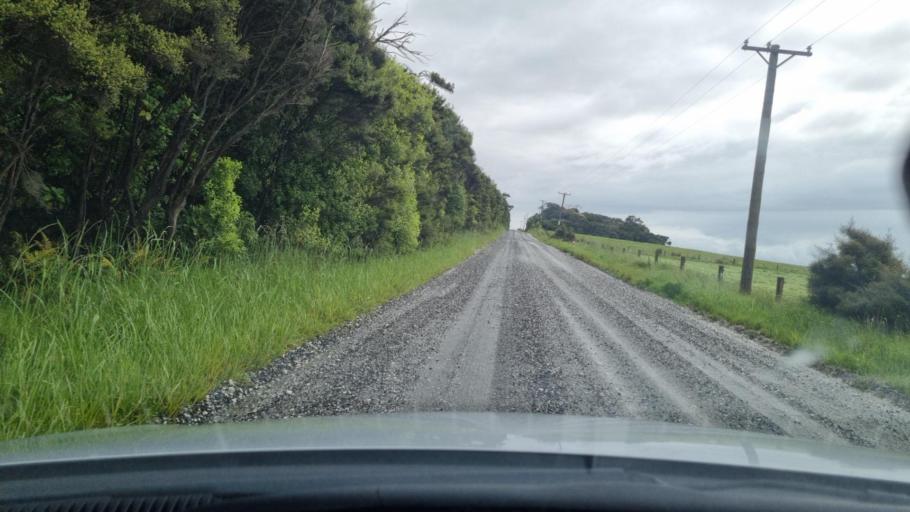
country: NZ
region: Southland
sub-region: Invercargill City
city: Bluff
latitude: -46.5307
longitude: 168.2681
